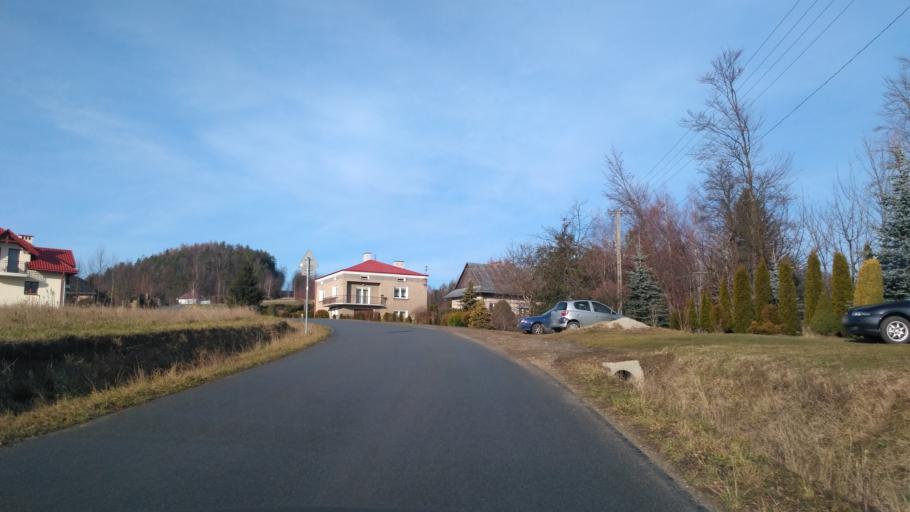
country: PL
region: Subcarpathian Voivodeship
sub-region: Powiat krosnienski
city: Korczyna
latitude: 49.7260
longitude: 21.7962
